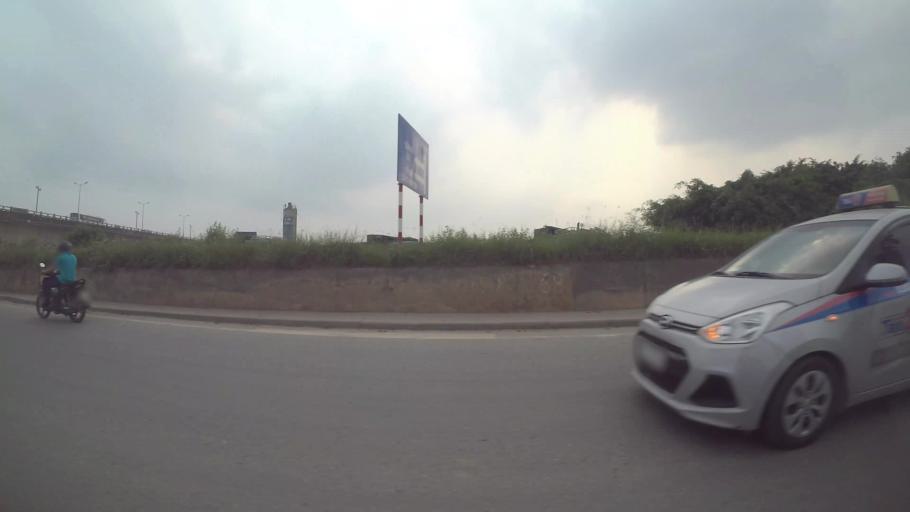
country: VN
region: Ha Noi
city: Trau Quy
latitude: 21.0031
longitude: 105.9093
